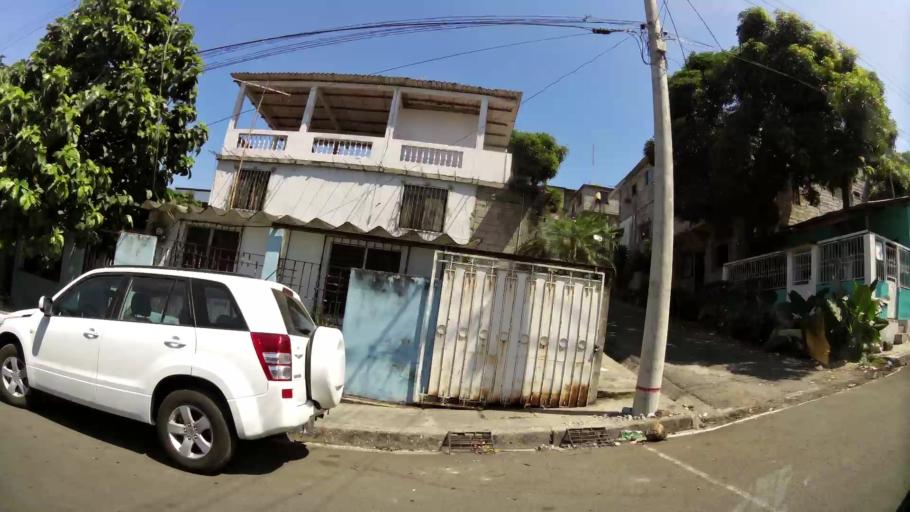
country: EC
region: Guayas
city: Guayaquil
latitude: -2.1850
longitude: -79.9285
